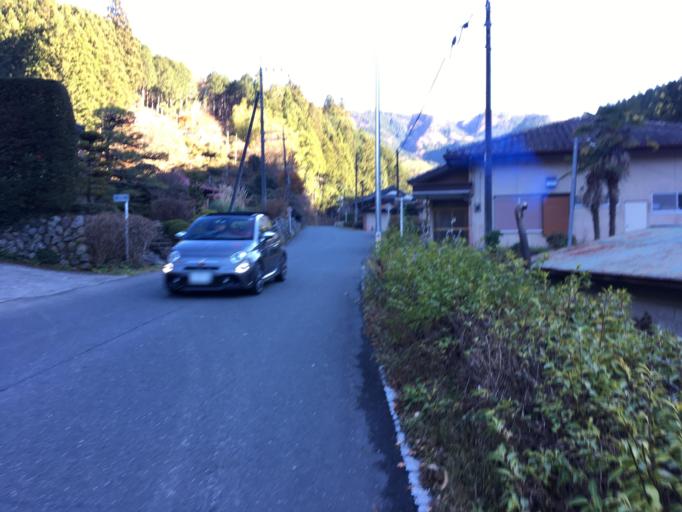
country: JP
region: Saitama
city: Chichibu
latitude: 36.0181
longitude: 139.1721
